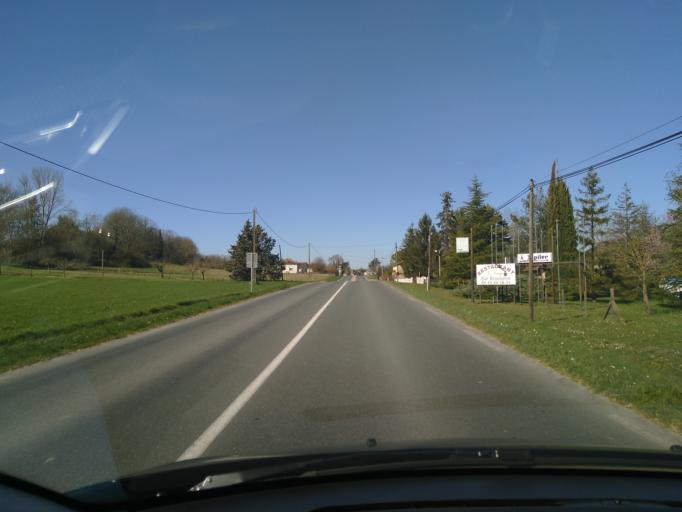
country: FR
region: Aquitaine
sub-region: Departement de la Dordogne
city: Monbazillac
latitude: 44.7536
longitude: 0.5313
